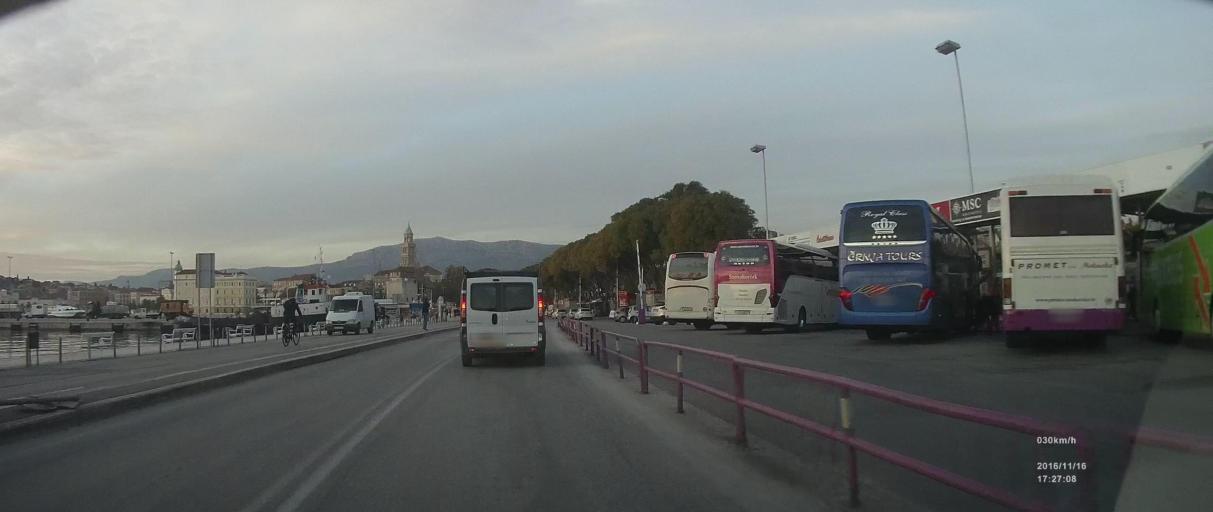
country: HR
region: Splitsko-Dalmatinska
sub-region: Grad Split
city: Split
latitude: 43.5038
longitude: 16.4428
